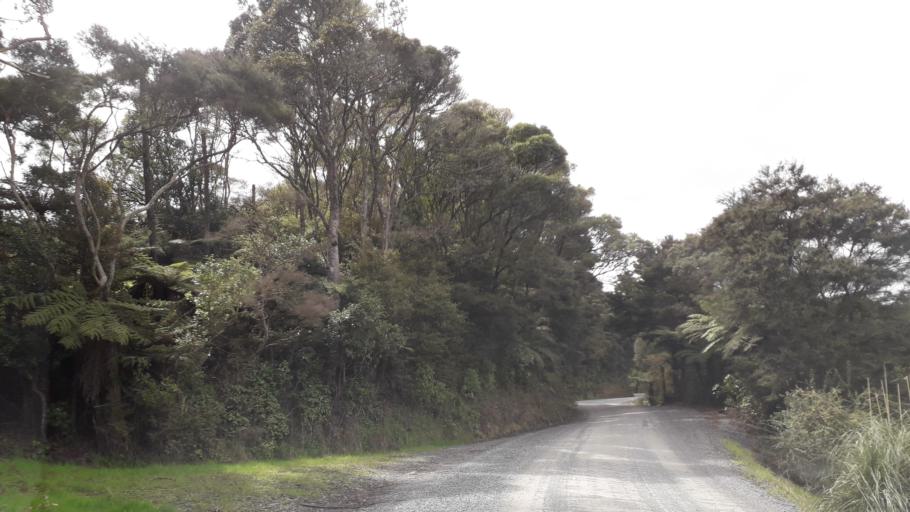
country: NZ
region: Northland
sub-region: Far North District
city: Kaitaia
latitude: -35.1697
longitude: 173.3368
